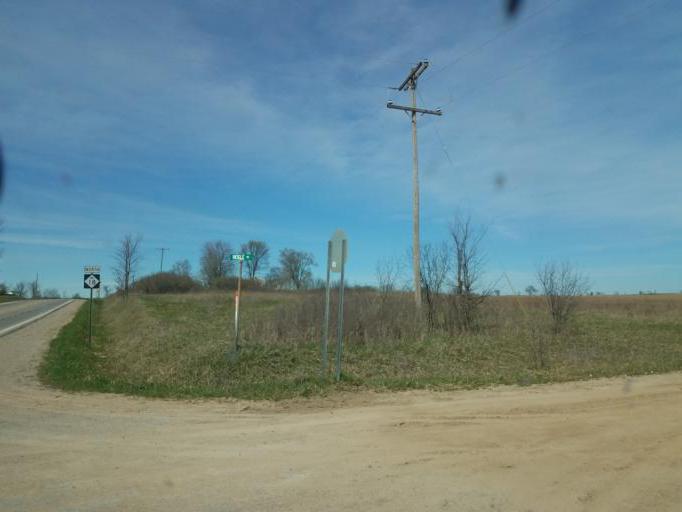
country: US
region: Michigan
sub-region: Gladwin County
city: Gladwin
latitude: 44.0598
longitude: -84.4866
